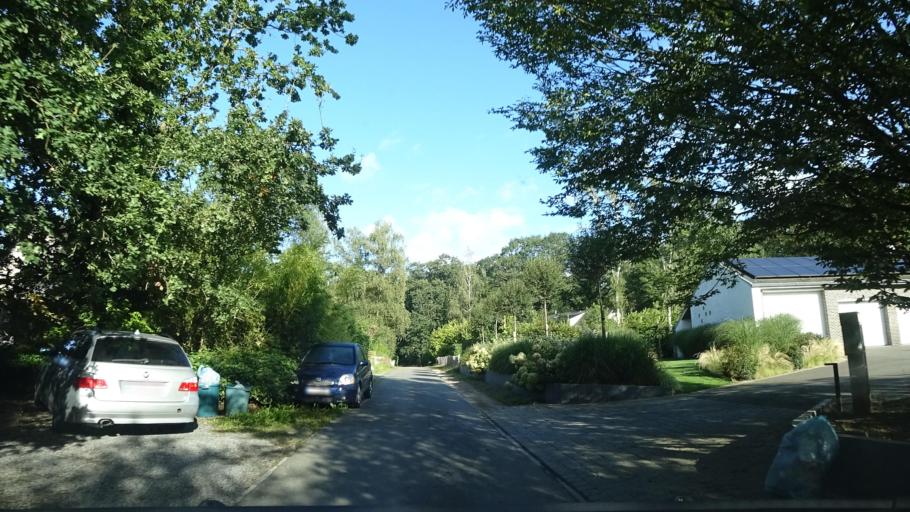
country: BE
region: Wallonia
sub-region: Province du Brabant Wallon
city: Court-Saint-Etienne
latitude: 50.6420
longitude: 4.5370
